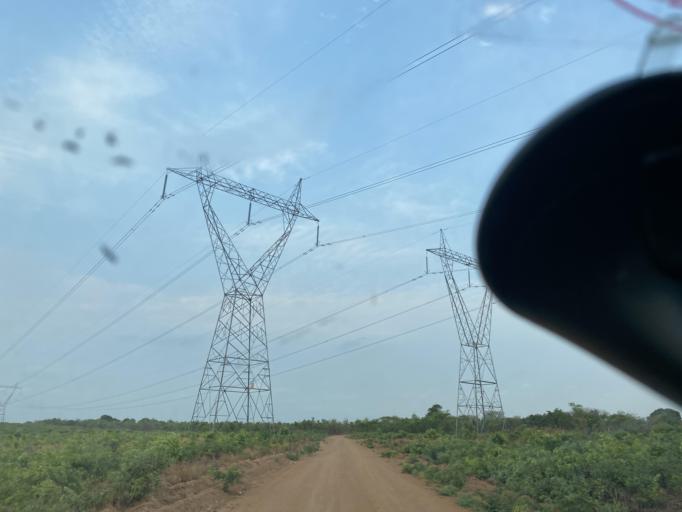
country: ZM
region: Lusaka
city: Chongwe
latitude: -15.2035
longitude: 28.5196
